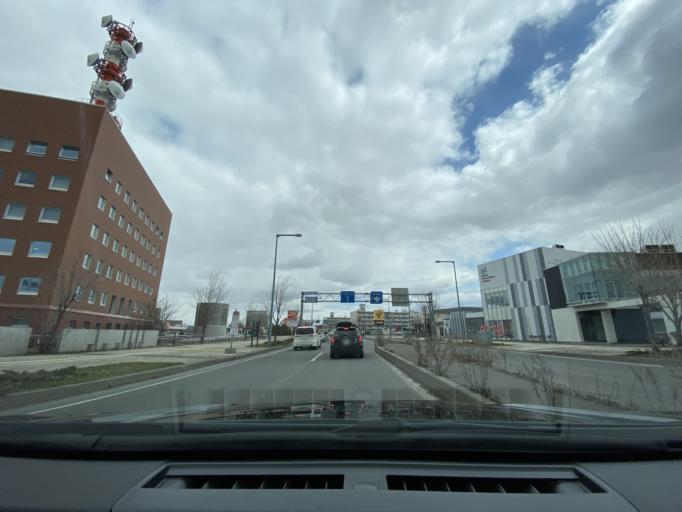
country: JP
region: Hokkaido
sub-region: Asahikawa-shi
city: Asahikawa
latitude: 43.7571
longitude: 142.3732
